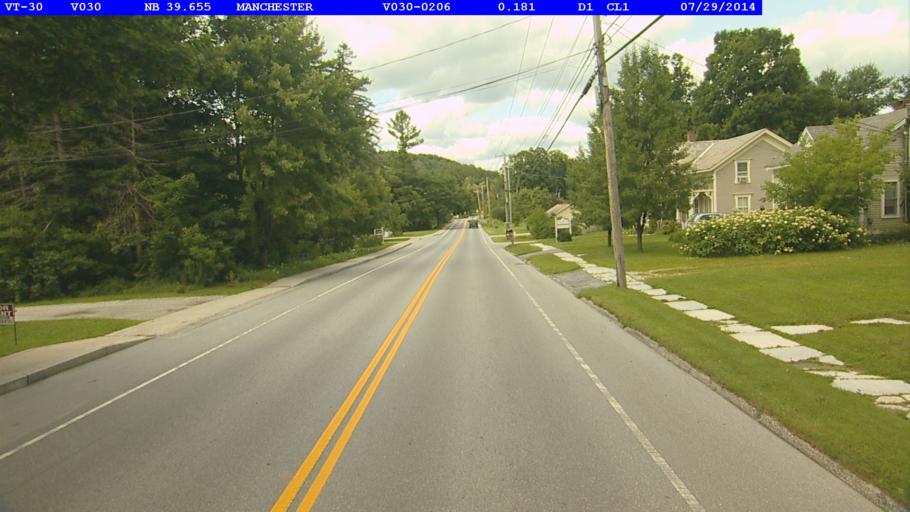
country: US
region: Vermont
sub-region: Bennington County
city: Manchester Center
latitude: 43.1794
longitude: -73.0574
